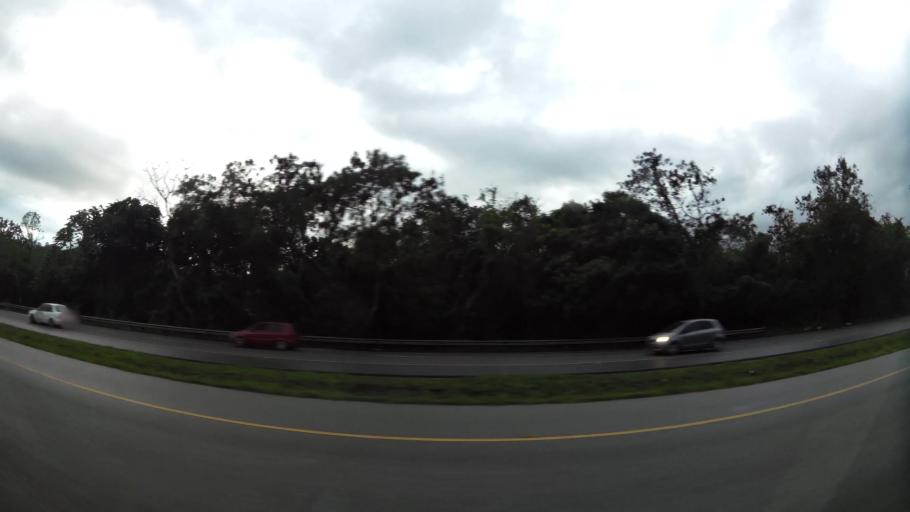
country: DO
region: San Cristobal
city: Villa Altagracia
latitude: 18.5905
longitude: -70.1267
